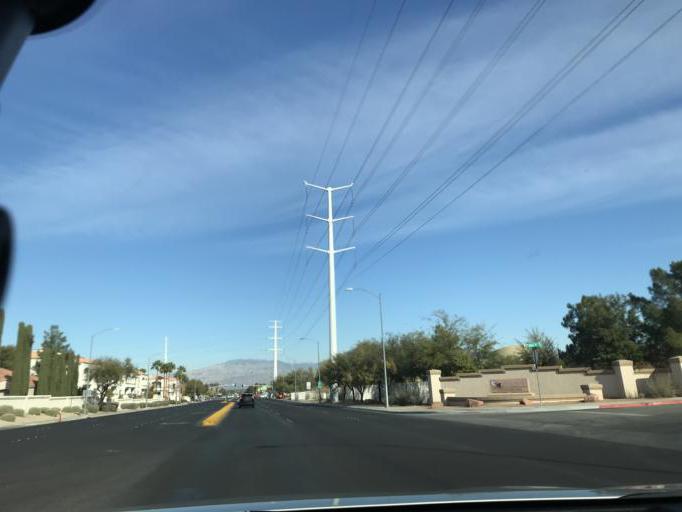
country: US
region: Nevada
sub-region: Clark County
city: Spring Valley
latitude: 36.2153
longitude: -115.2604
